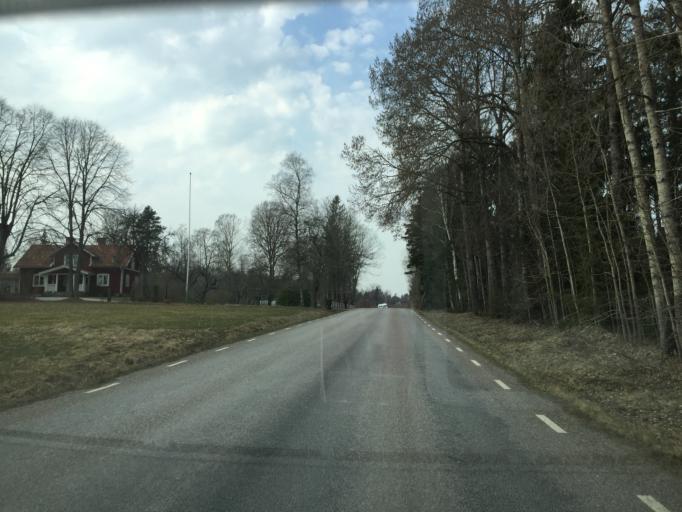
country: SE
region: Soedermanland
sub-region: Vingakers Kommun
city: Vingaker
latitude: 59.0463
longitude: 15.7816
